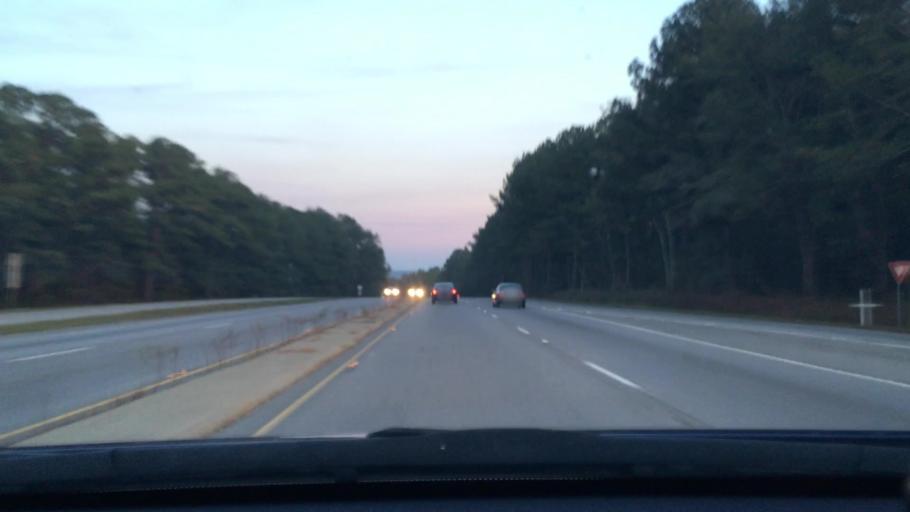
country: US
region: South Carolina
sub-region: Richland County
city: Gadsden
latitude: 33.9425
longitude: -80.6853
